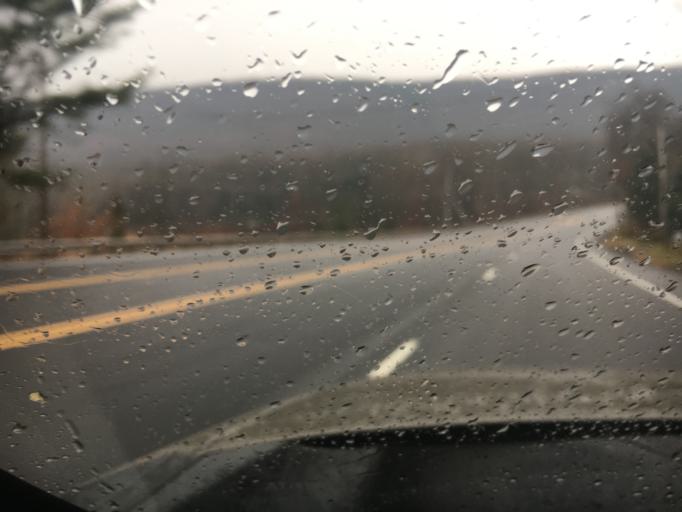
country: US
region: Pennsylvania
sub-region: Luzerne County
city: Oakdale
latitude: 41.0356
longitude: -75.9529
